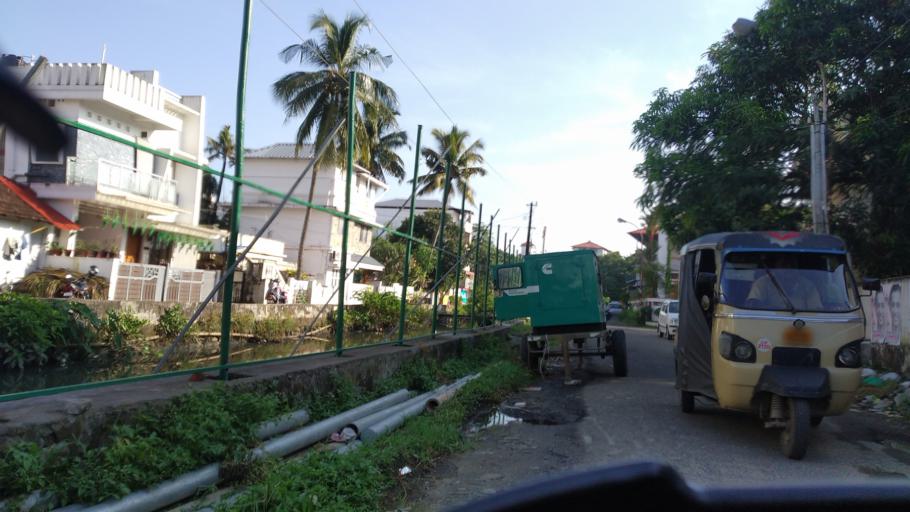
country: IN
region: Kerala
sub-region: Ernakulam
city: Cochin
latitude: 9.9871
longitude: 76.2913
